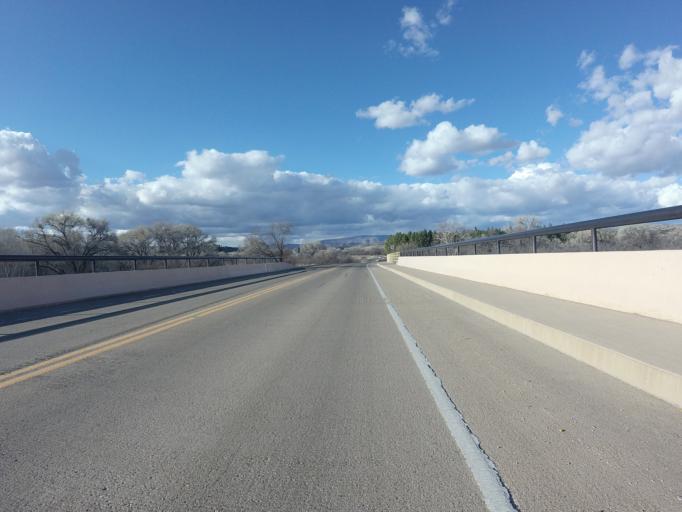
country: US
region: Arizona
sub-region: Yavapai County
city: Cottonwood
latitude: 34.7509
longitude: -112.0221
